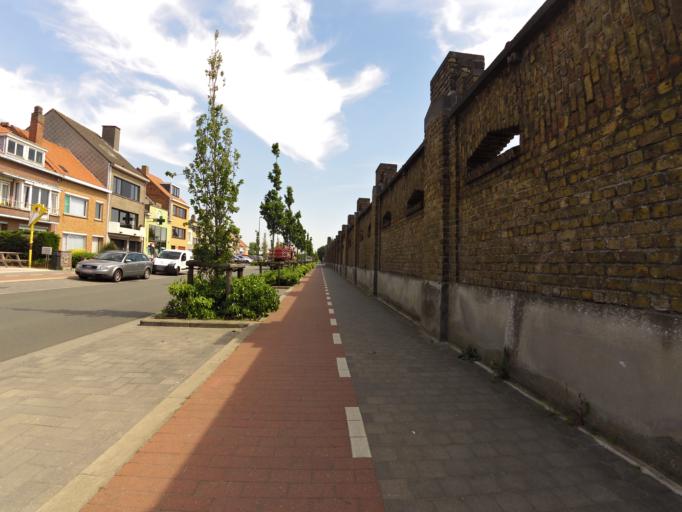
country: BE
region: Flanders
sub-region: Provincie West-Vlaanderen
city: Ostend
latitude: 51.2106
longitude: 2.9149
